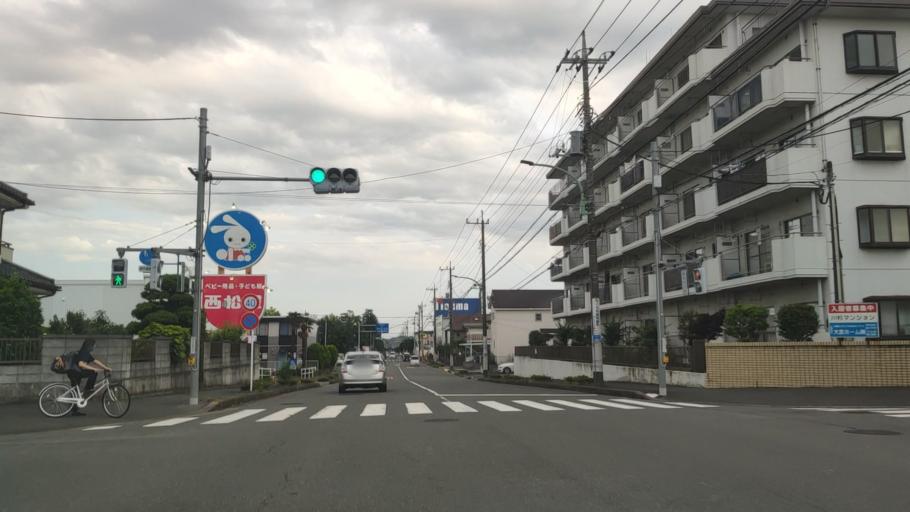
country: JP
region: Tokyo
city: Ome
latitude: 35.7931
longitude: 139.2987
